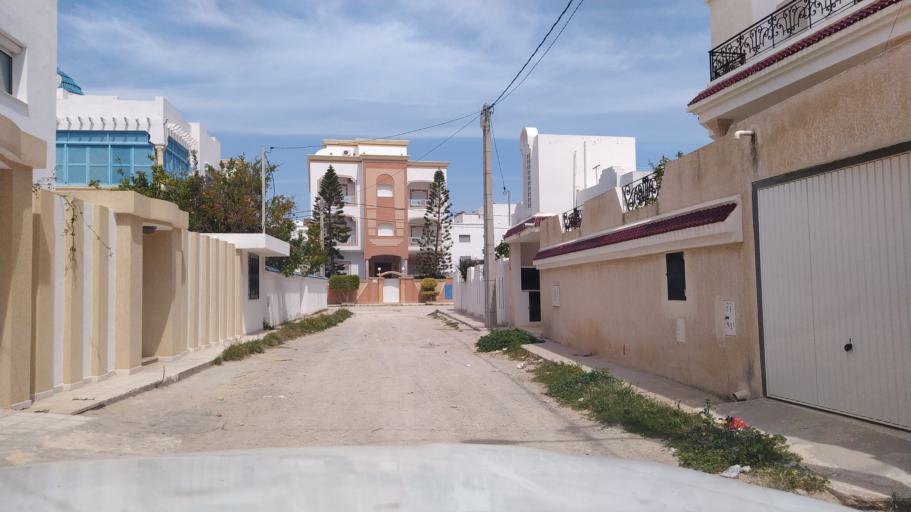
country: TN
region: Al Mahdiyah
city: Mahdia
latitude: 35.5210
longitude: 11.0402
